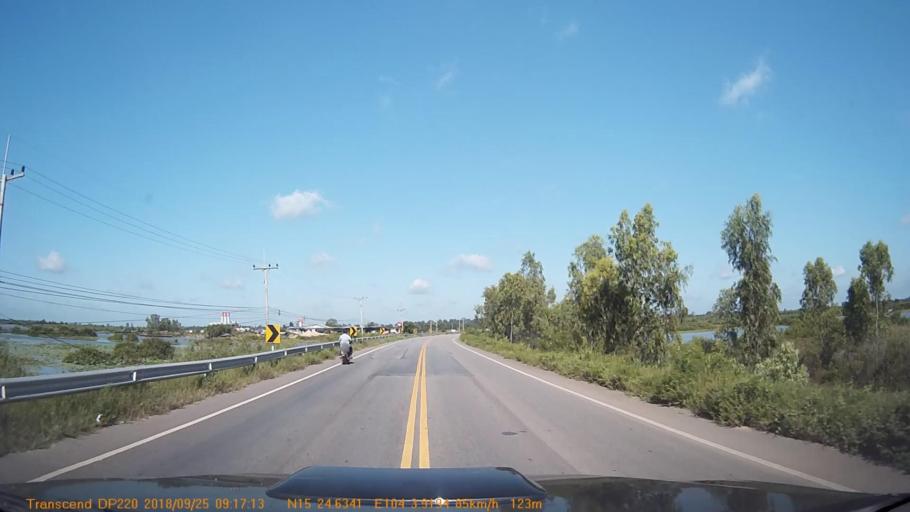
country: TH
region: Sisaket
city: Sila Lat
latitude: 15.4105
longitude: 104.0654
